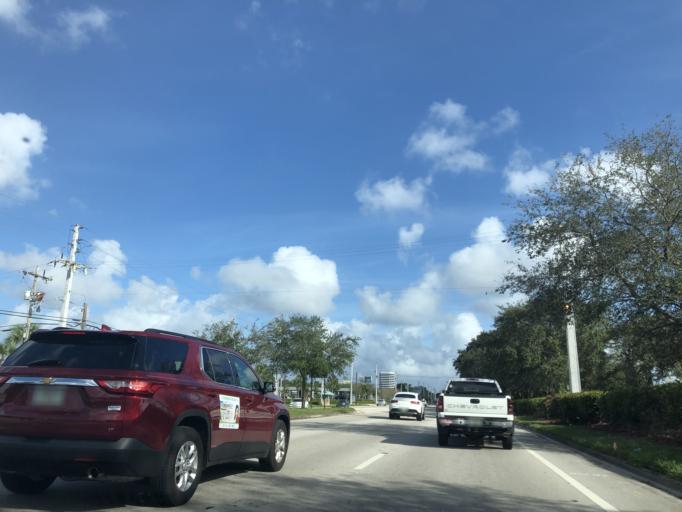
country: US
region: Florida
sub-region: Palm Beach County
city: Haverhill
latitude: 26.6911
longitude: -80.0855
